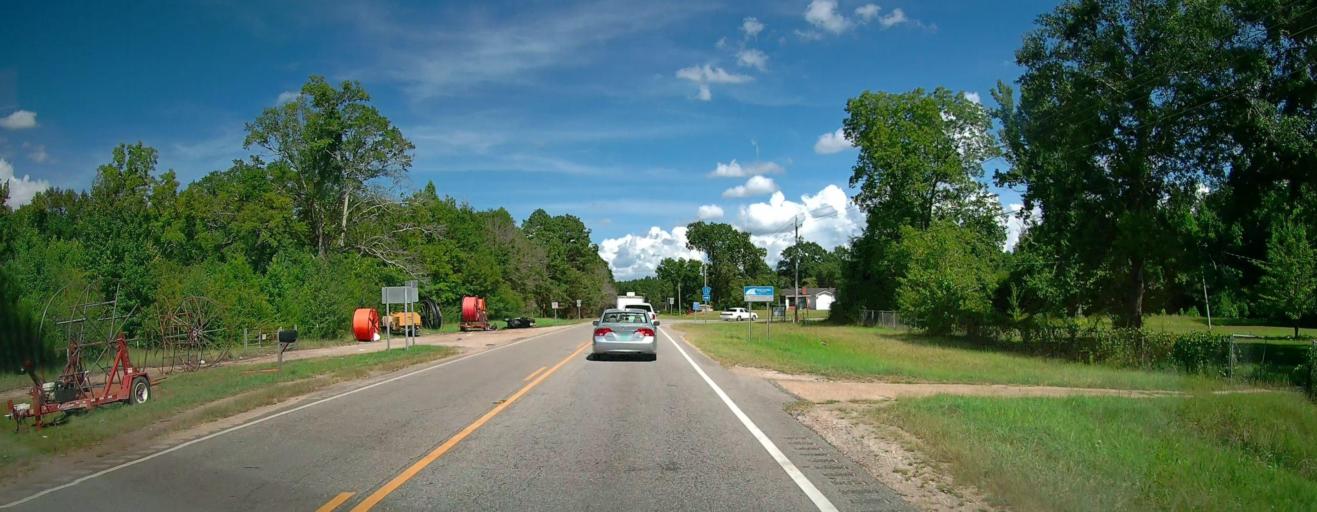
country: US
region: Alabama
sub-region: Elmore County
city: Tallassee
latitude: 32.3761
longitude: -85.8506
